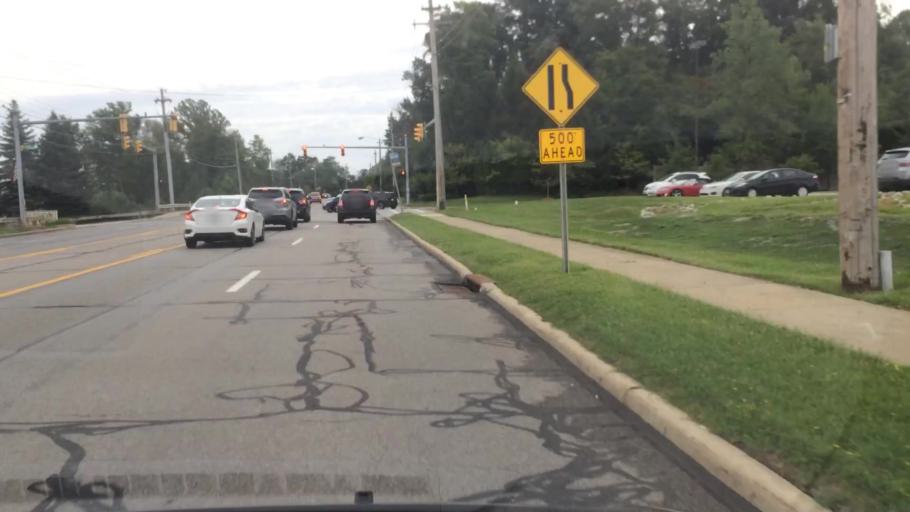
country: US
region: Ohio
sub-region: Cuyahoga County
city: Strongsville
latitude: 41.3084
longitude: -81.8139
